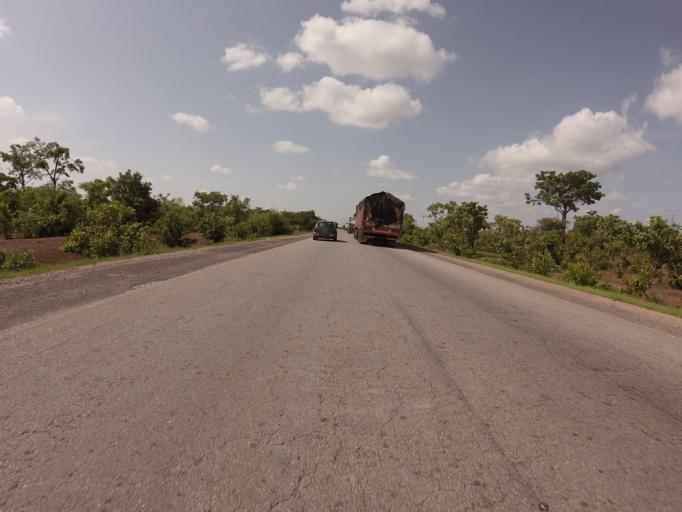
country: GH
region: Northern
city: Savelugu
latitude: 9.9538
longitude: -0.8353
